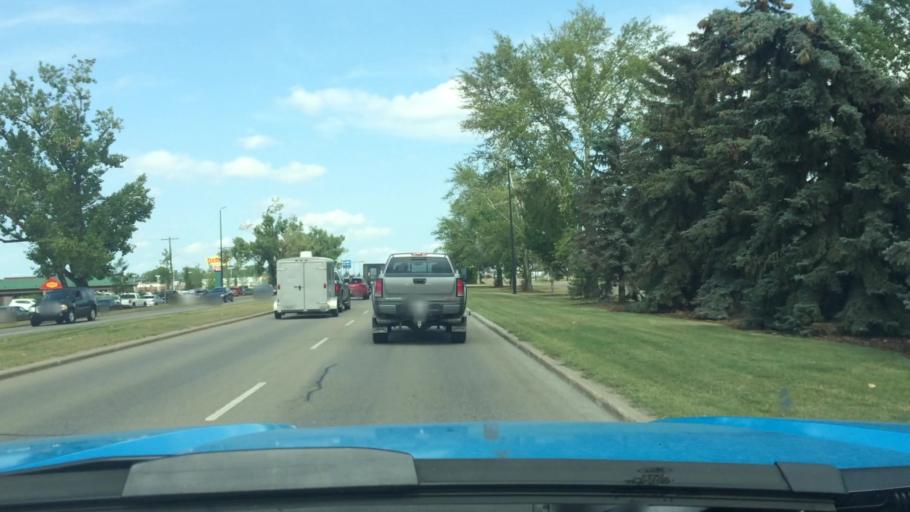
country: CA
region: Alberta
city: Red Deer
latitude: 52.2460
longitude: -113.8139
